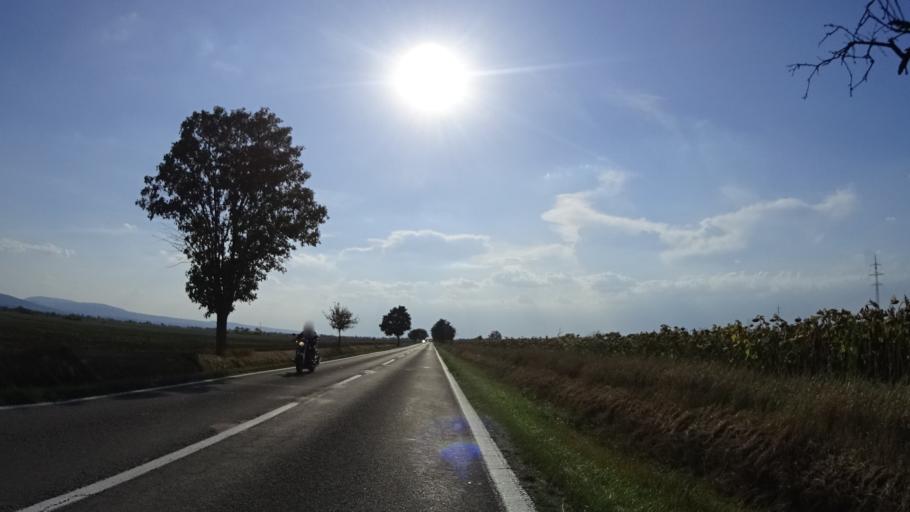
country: HU
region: Komarom-Esztergom
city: Tat
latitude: 47.7913
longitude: 18.6488
